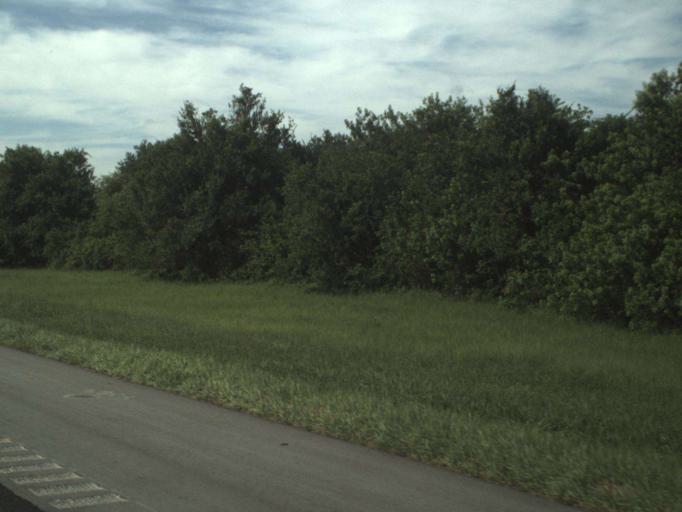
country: US
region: Florida
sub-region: Indian River County
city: West Vero Corridor
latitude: 27.5966
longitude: -80.5049
